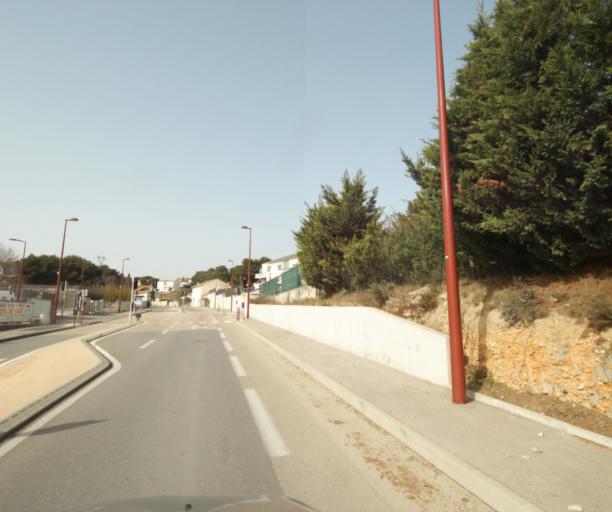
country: FR
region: Provence-Alpes-Cote d'Azur
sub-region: Departement des Bouches-du-Rhone
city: Septemes-les-Vallons
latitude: 43.4002
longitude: 5.3408
